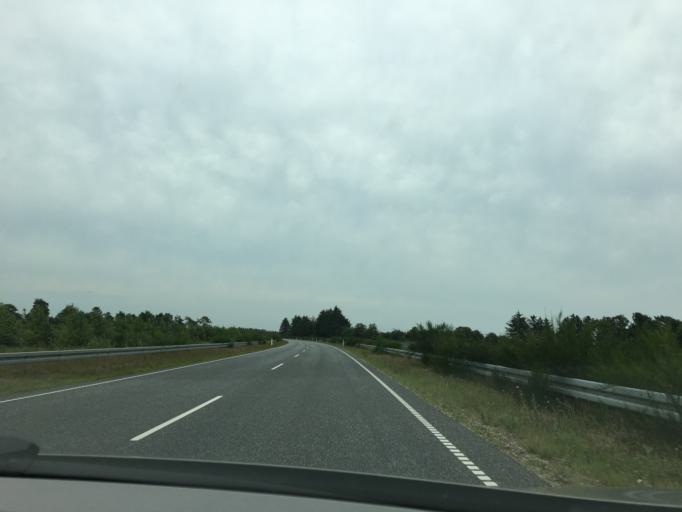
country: DK
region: Central Jutland
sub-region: Herning Kommune
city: Sunds
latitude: 56.1973
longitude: 8.9955
